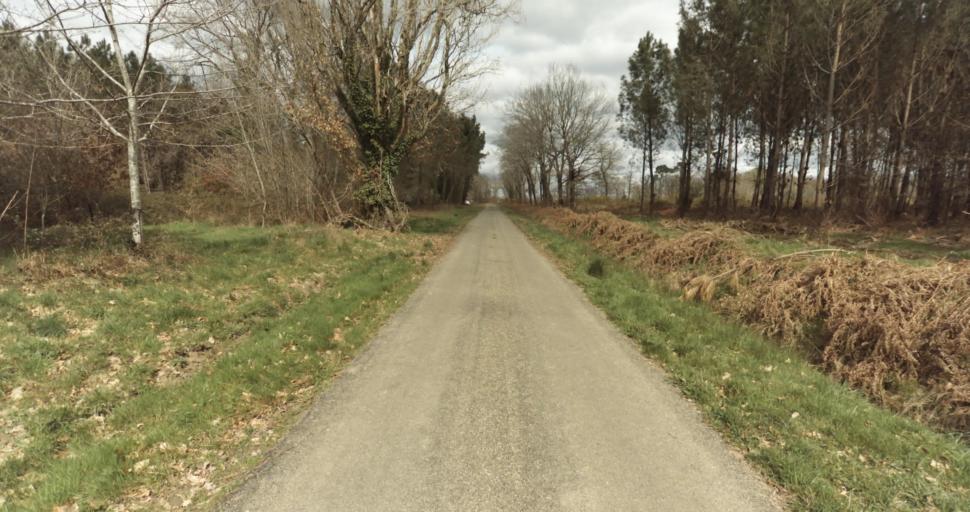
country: FR
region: Aquitaine
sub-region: Departement des Landes
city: Roquefort
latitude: 44.0728
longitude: -0.4129
